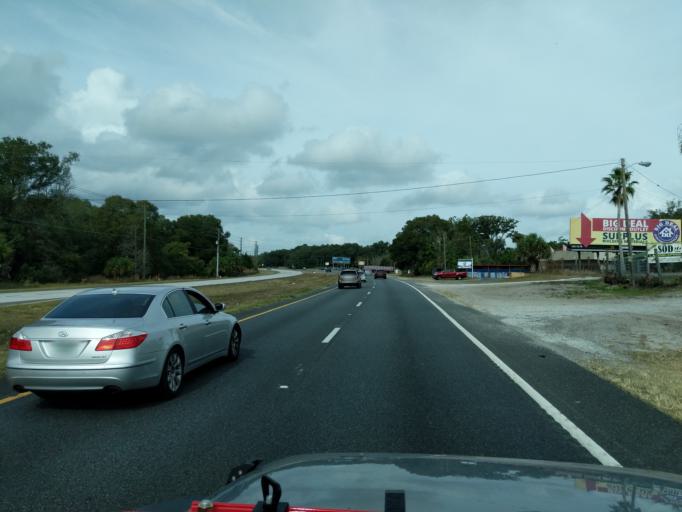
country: US
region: Florida
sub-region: Orange County
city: Zellwood
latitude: 28.7427
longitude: -81.6161
